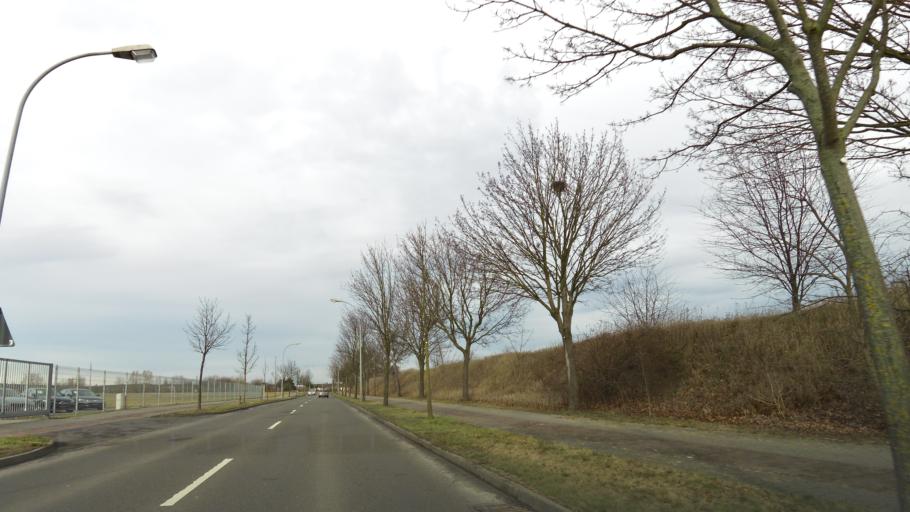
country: DE
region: Brandenburg
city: Strausberg
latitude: 52.5814
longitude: 13.9084
